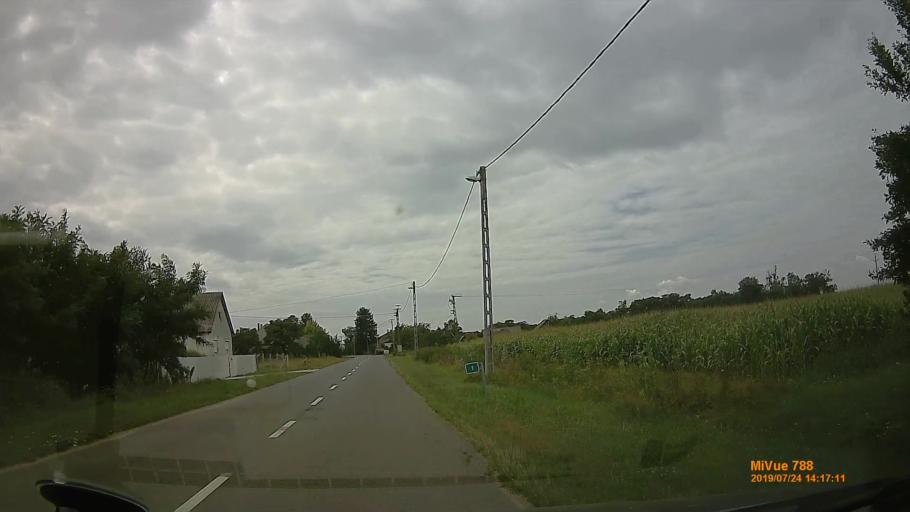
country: HU
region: Szabolcs-Szatmar-Bereg
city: Mandok
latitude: 48.3149
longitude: 22.2863
